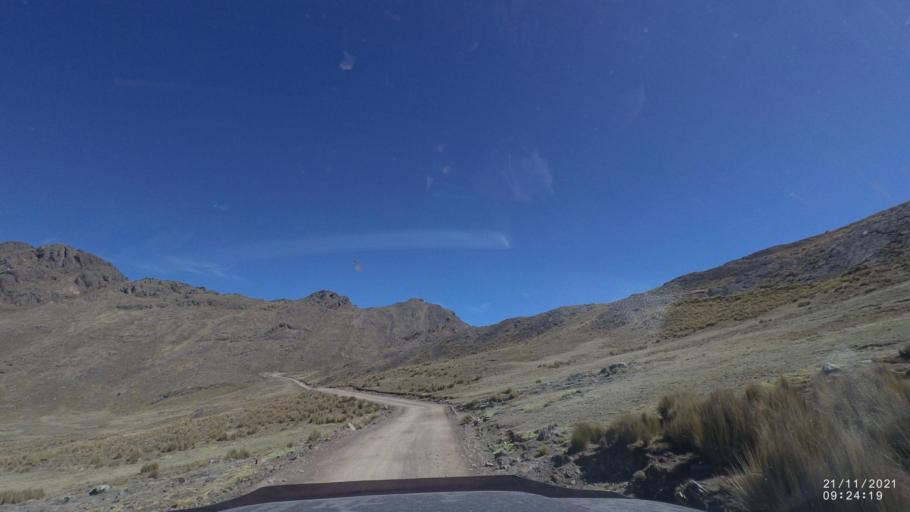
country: BO
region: Cochabamba
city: Cochabamba
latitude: -17.0929
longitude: -66.2546
